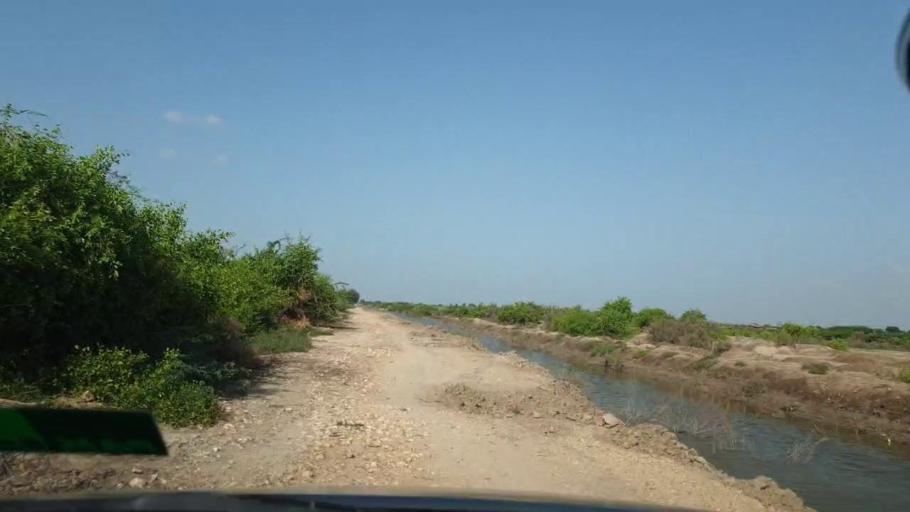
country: PK
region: Sindh
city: Tando Bago
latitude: 24.7004
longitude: 69.1987
